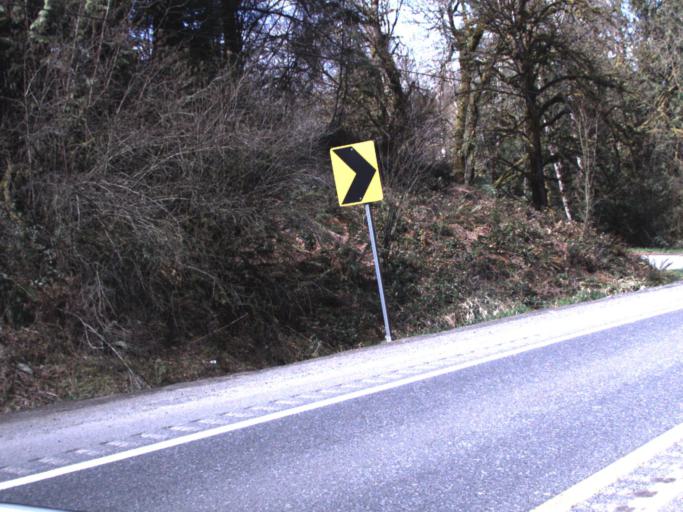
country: US
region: Washington
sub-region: King County
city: Black Diamond
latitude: 47.2702
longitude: -121.9934
